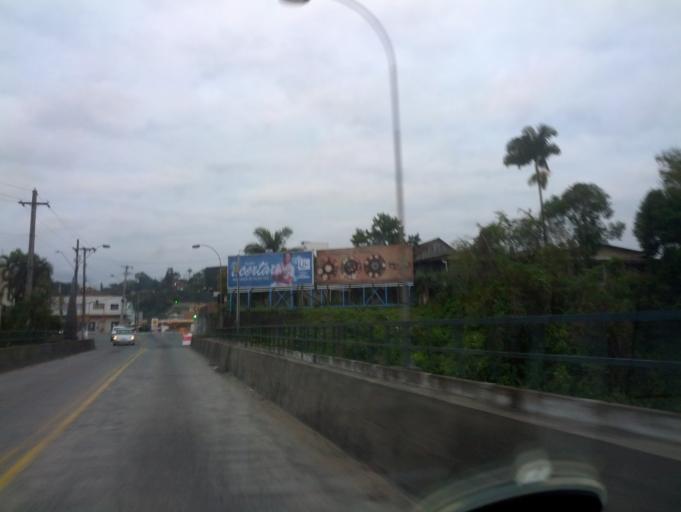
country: BR
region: Santa Catarina
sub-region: Blumenau
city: Blumenau
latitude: -26.8876
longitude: -49.0843
